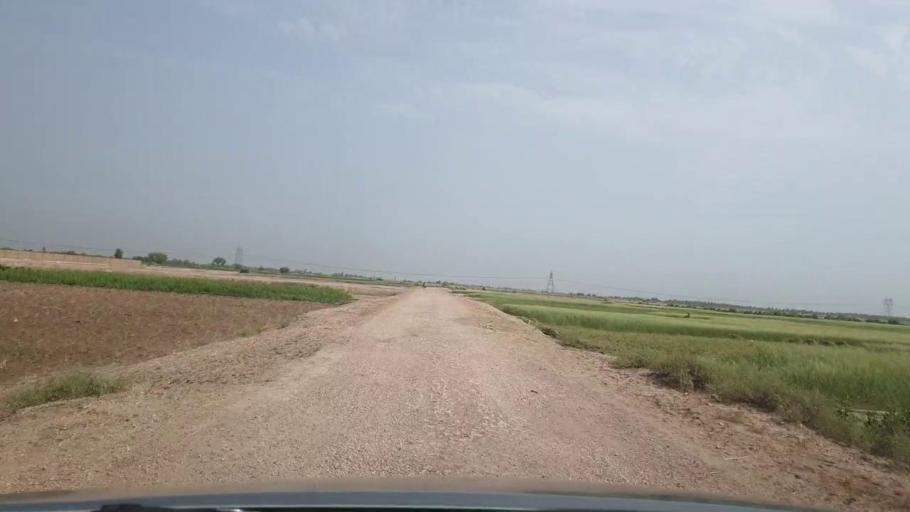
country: PK
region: Sindh
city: Rohri
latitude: 27.6661
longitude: 69.0259
